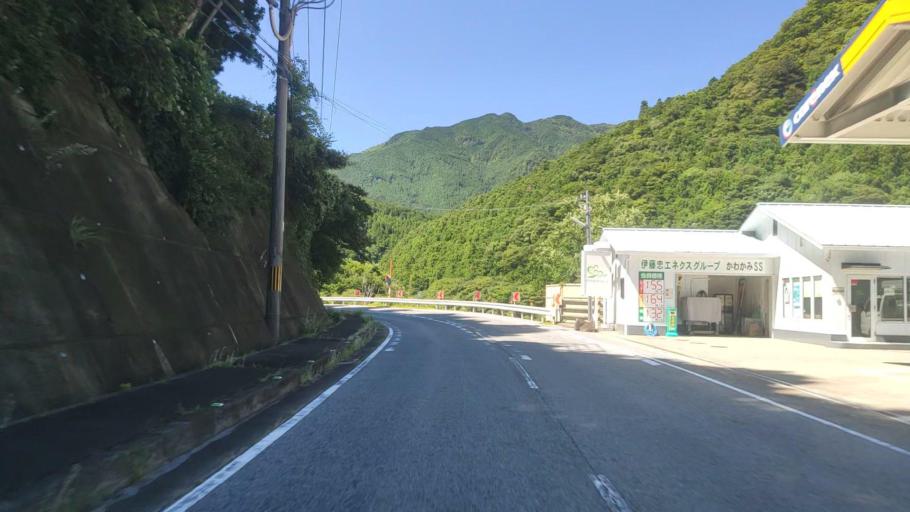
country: JP
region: Nara
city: Yoshino-cho
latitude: 34.3220
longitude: 135.9706
